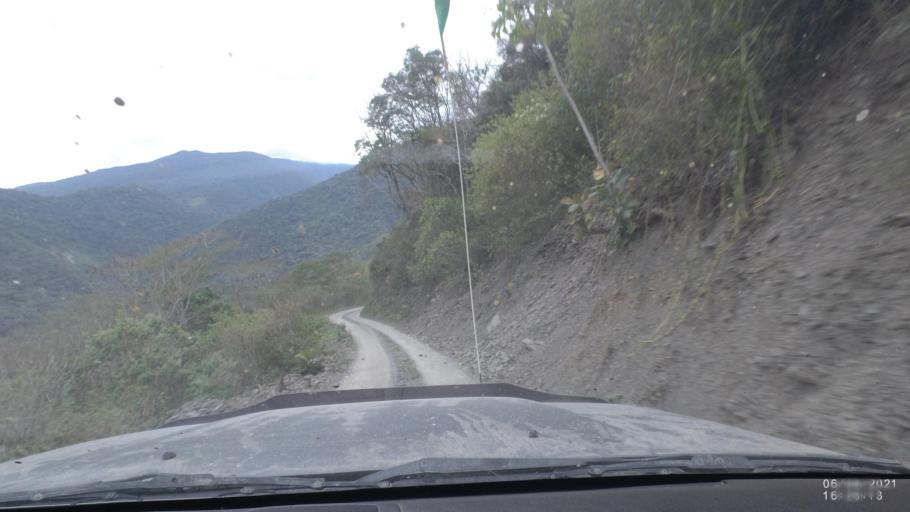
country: BO
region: La Paz
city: Quime
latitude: -16.5332
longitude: -66.7577
